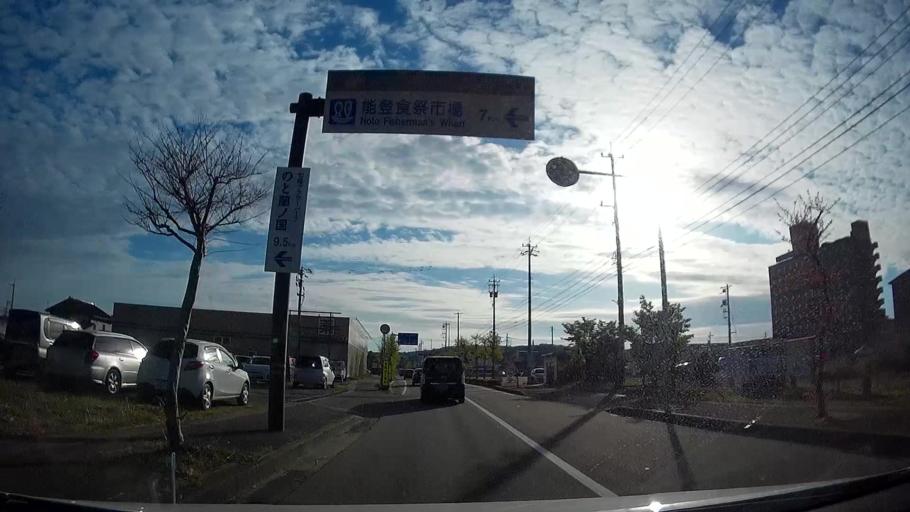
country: JP
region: Ishikawa
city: Nanao
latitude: 37.0839
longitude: 136.9280
